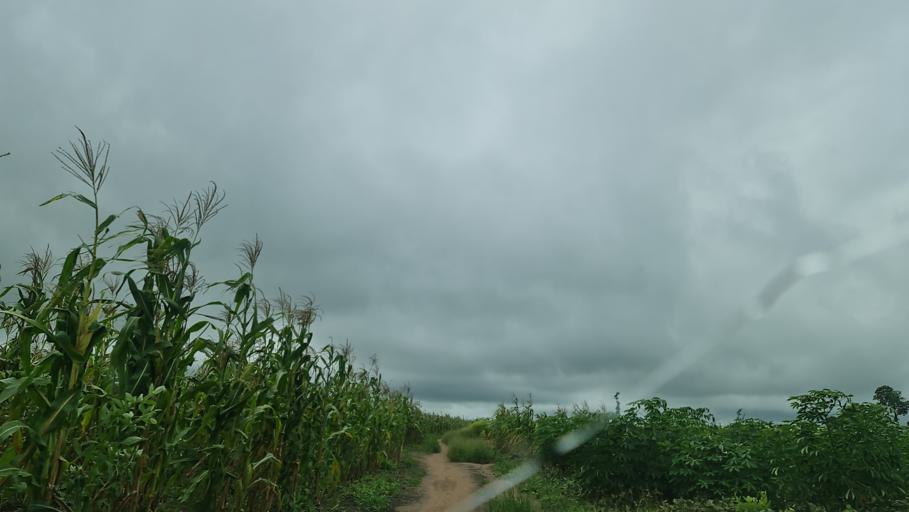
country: MW
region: Southern Region
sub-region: Nsanje District
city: Nsanje
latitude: -17.3413
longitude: 35.7321
